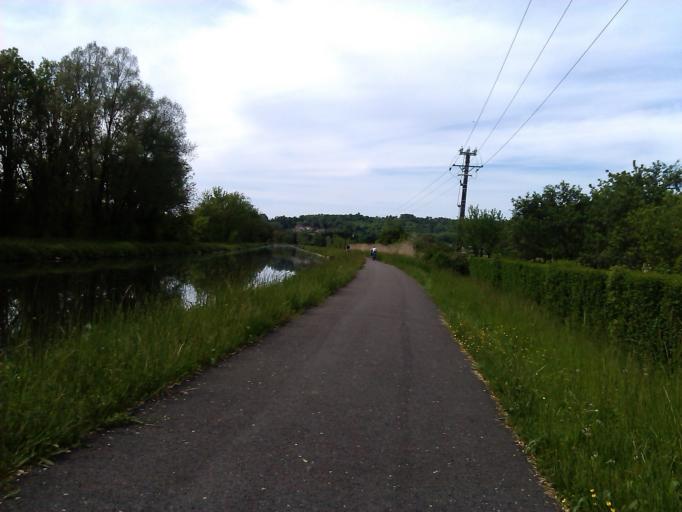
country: FR
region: Franche-Comte
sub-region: Departement du Doubs
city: Boussieres
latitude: 47.1575
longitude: 5.8562
